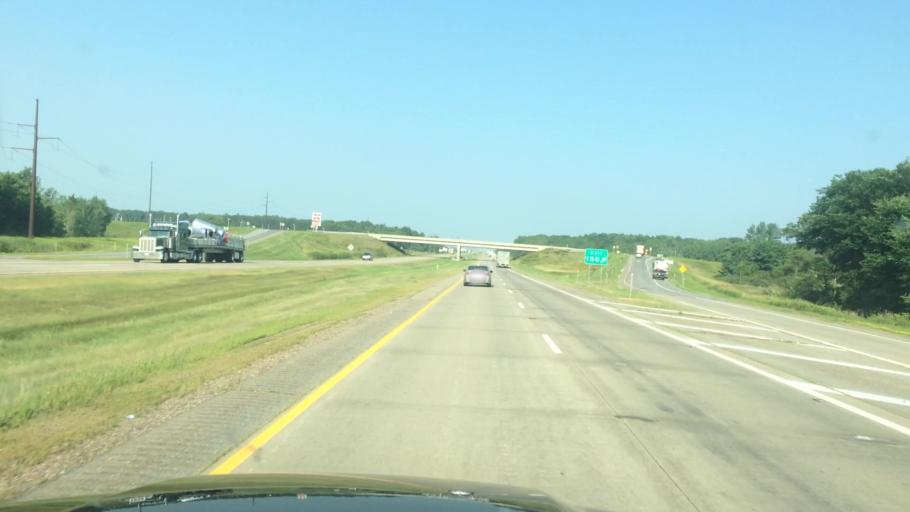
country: US
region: Wisconsin
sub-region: Marathon County
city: Edgar
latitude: 44.9445
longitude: -89.9593
